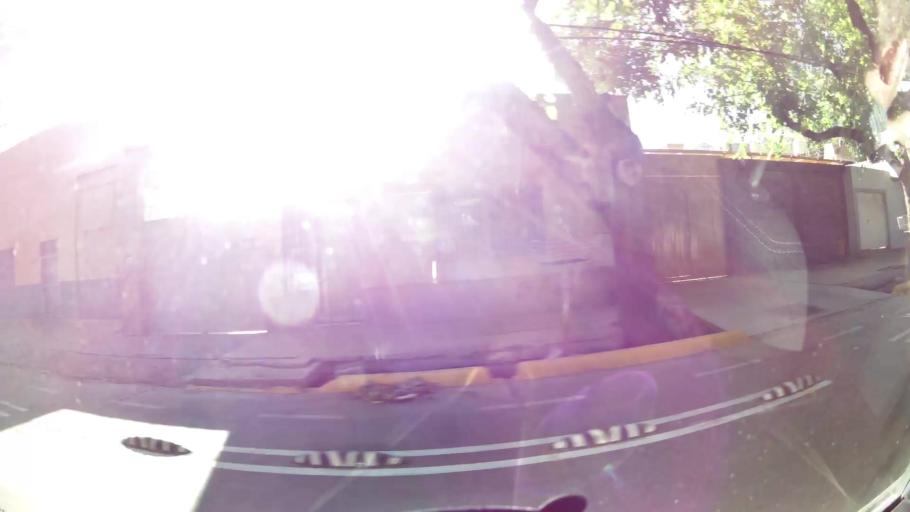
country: AR
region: Mendoza
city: Las Heras
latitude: -32.8684
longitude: -68.8256
